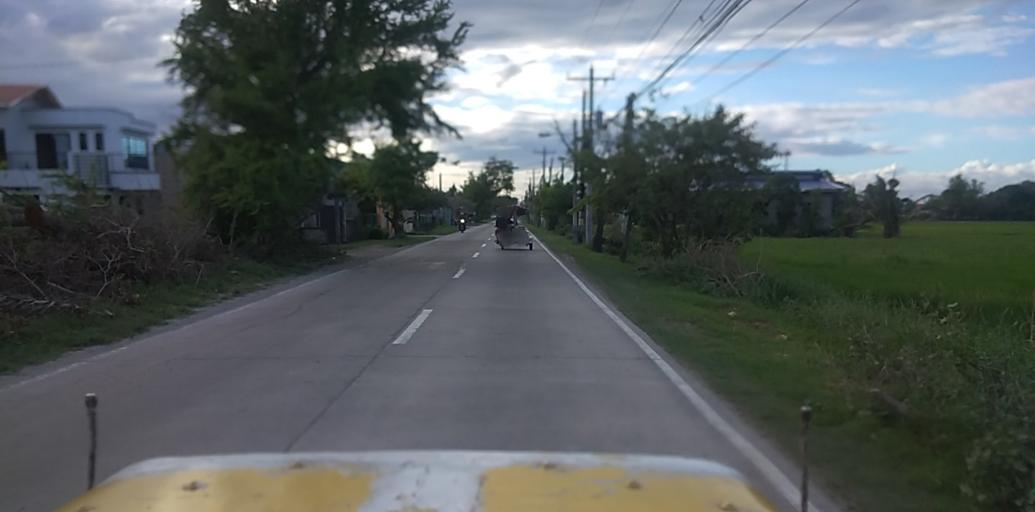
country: PH
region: Central Luzon
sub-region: Province of Pampanga
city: Arayat
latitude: 15.1533
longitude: 120.7319
